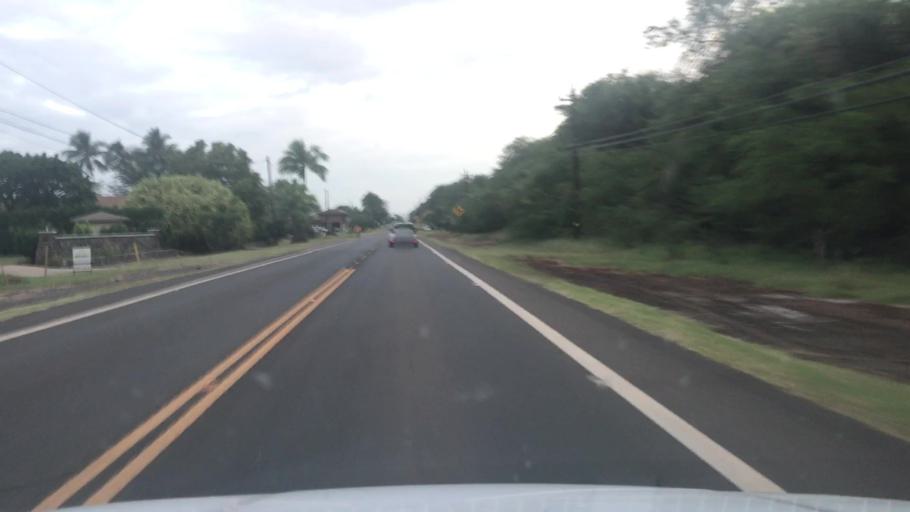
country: US
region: Hawaii
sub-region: Maui County
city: Kaunakakai
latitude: 21.0700
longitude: -156.9663
